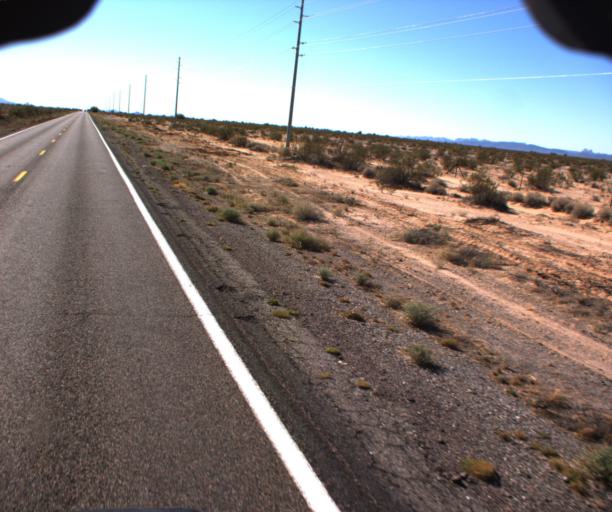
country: US
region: Arizona
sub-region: La Paz County
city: Quartzsite
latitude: 33.8920
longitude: -113.9614
